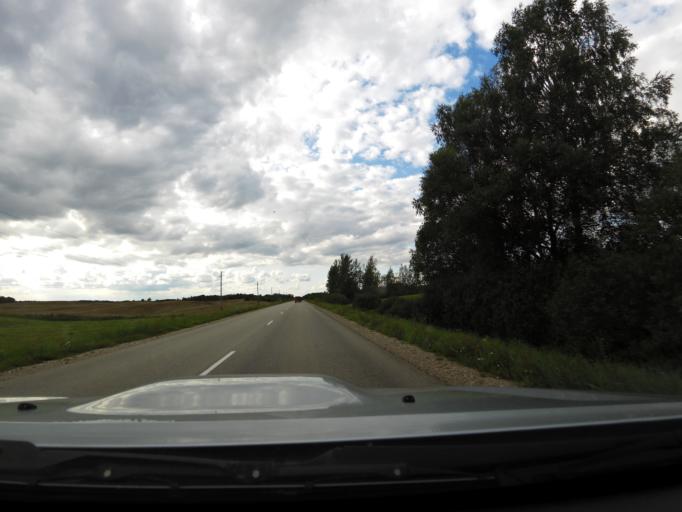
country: LV
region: Akniste
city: Akniste
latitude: 55.9870
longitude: 25.9851
